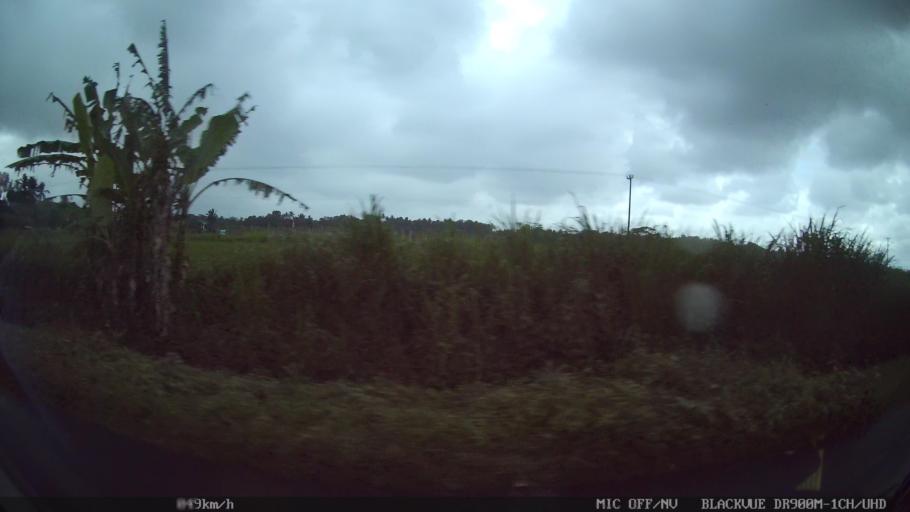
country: ID
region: Bali
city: Banjar Badung Tengah
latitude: -8.5125
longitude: 115.1988
